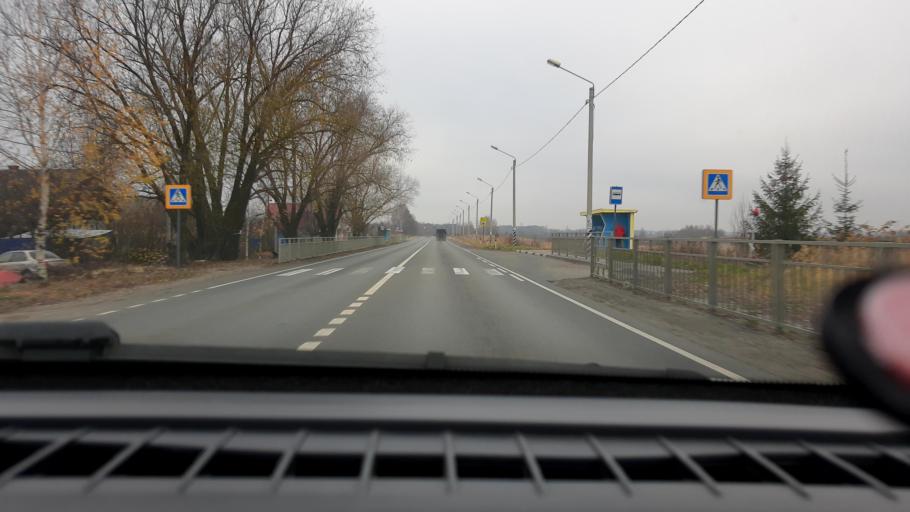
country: RU
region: Nizjnij Novgorod
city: Gidrotorf
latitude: 56.5536
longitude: 43.5157
